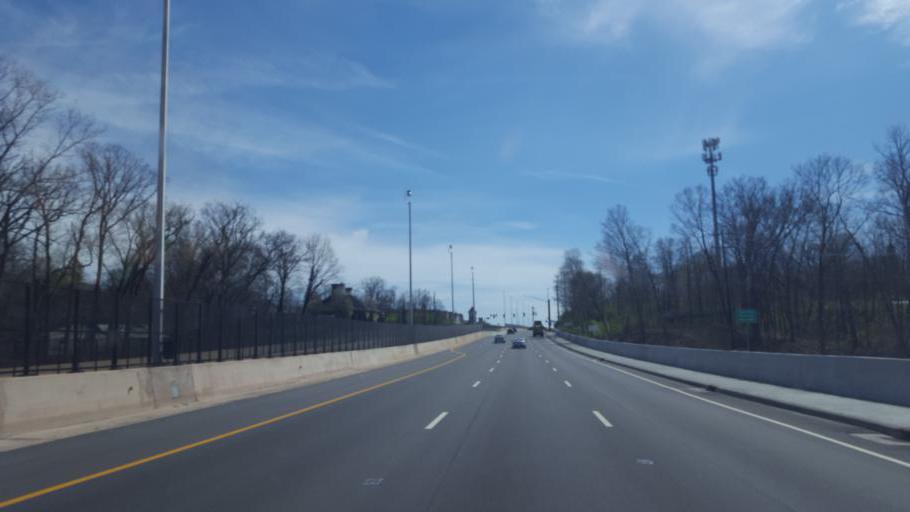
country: US
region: Ohio
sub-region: Franklin County
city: Worthington
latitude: 40.1245
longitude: -83.0162
